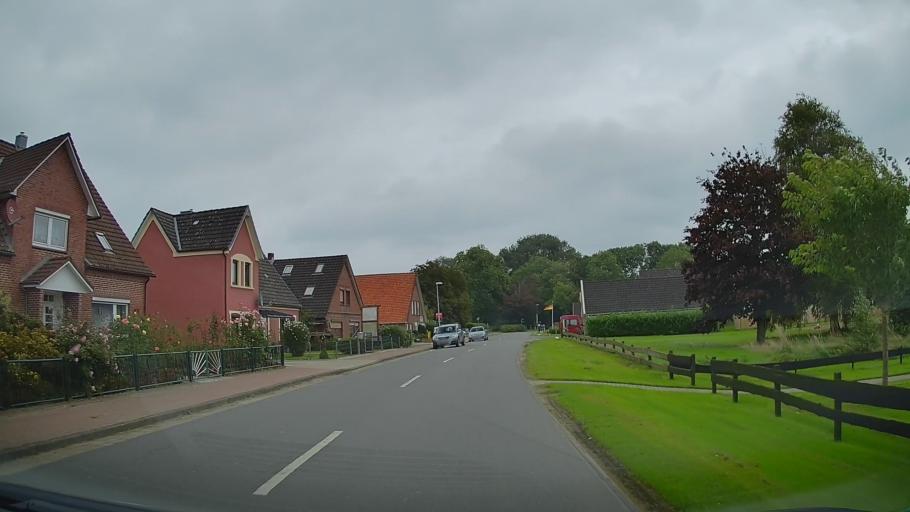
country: DE
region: Lower Saxony
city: Geversdorf
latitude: 53.8213
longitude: 9.0877
